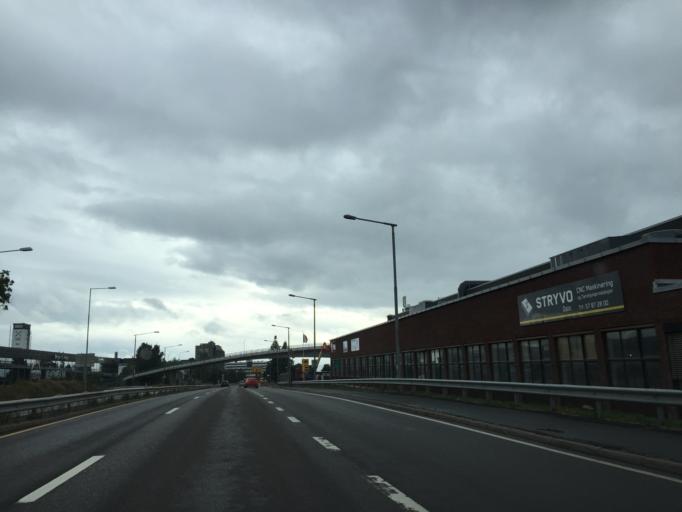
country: NO
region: Oslo
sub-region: Oslo
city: Oslo
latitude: 59.9320
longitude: 10.8258
